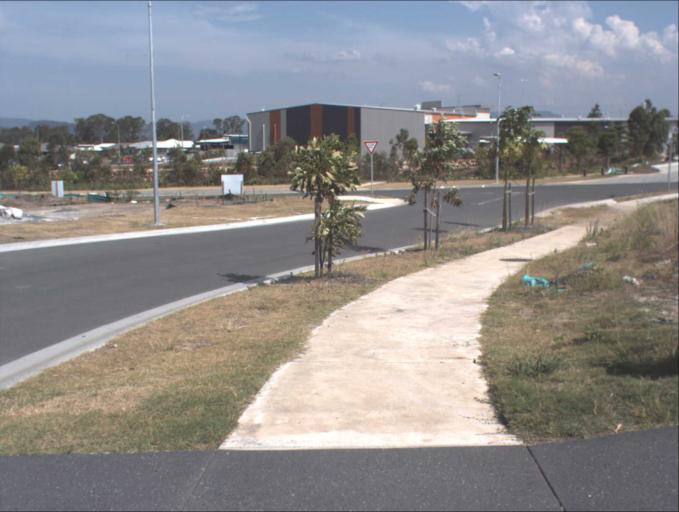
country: AU
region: Queensland
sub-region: Logan
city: Chambers Flat
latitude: -27.8000
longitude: 153.1016
